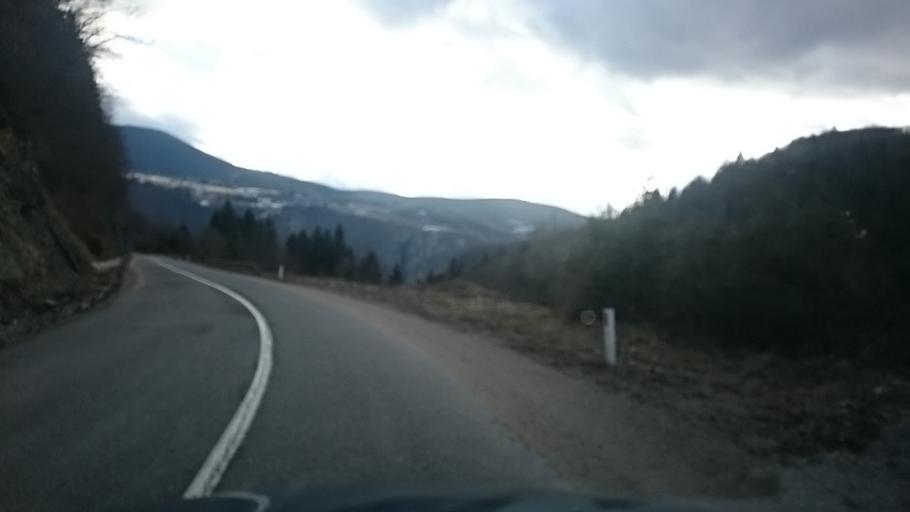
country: BA
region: Republika Srpska
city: Skender Vakuf
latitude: 44.4673
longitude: 17.3744
